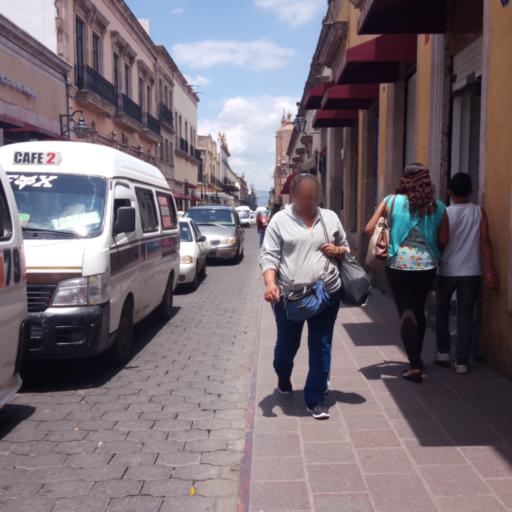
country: MX
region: Michoacan
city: Morelia
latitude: 19.7019
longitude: -101.1907
